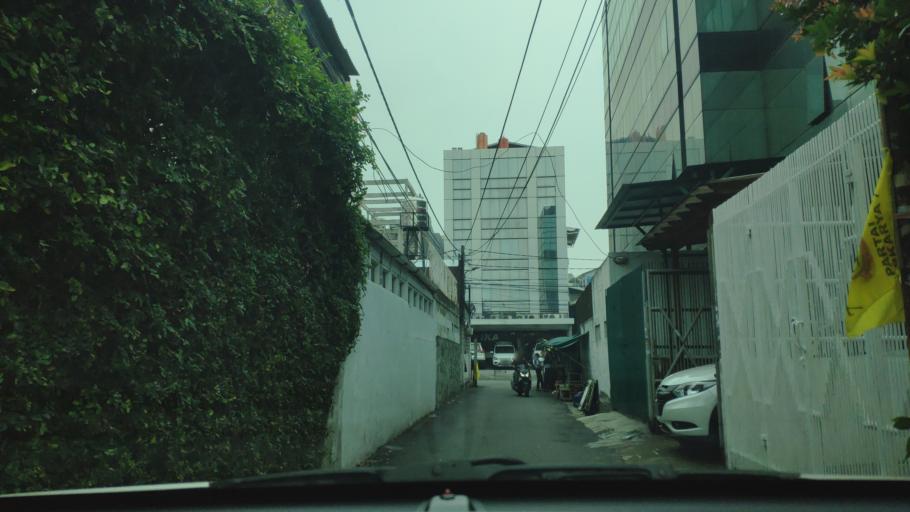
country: ID
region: Jakarta Raya
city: Jakarta
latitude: -6.1674
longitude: 106.8157
